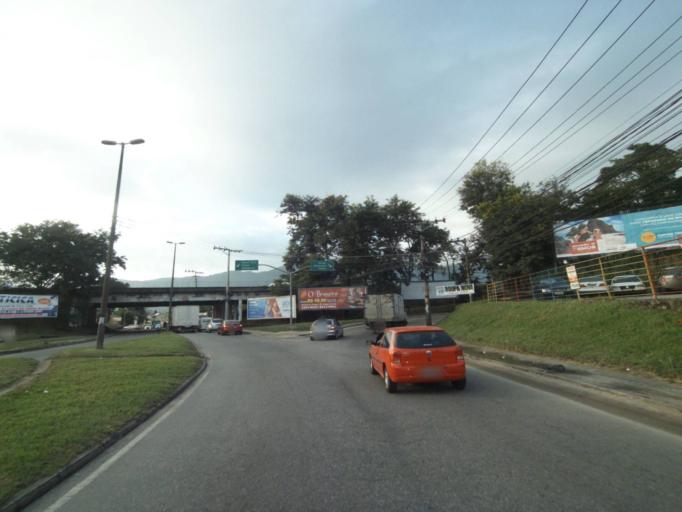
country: BR
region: Rio de Janeiro
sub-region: Nova Iguacu
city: Nova Iguacu
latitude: -22.8621
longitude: -43.5412
